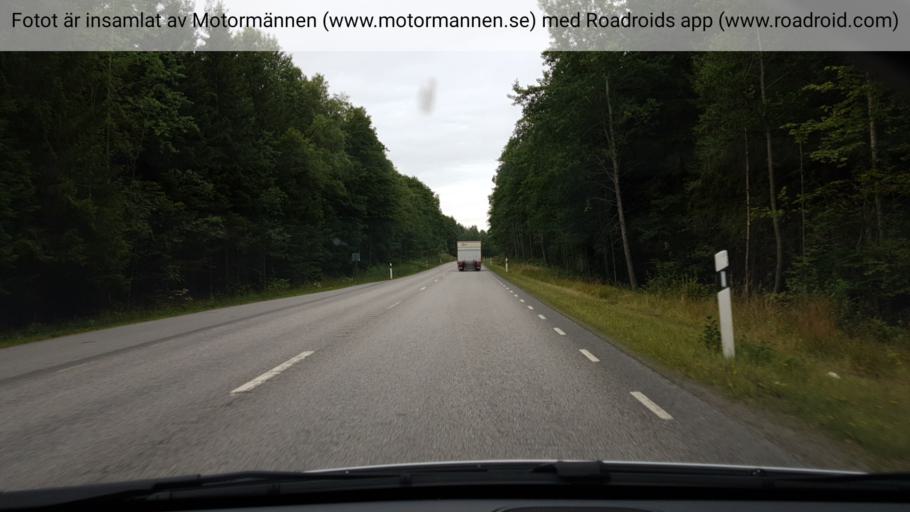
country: SE
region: Vaestra Goetaland
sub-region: Karlsborgs Kommun
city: Molltorp
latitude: 58.4839
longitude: 14.3537
